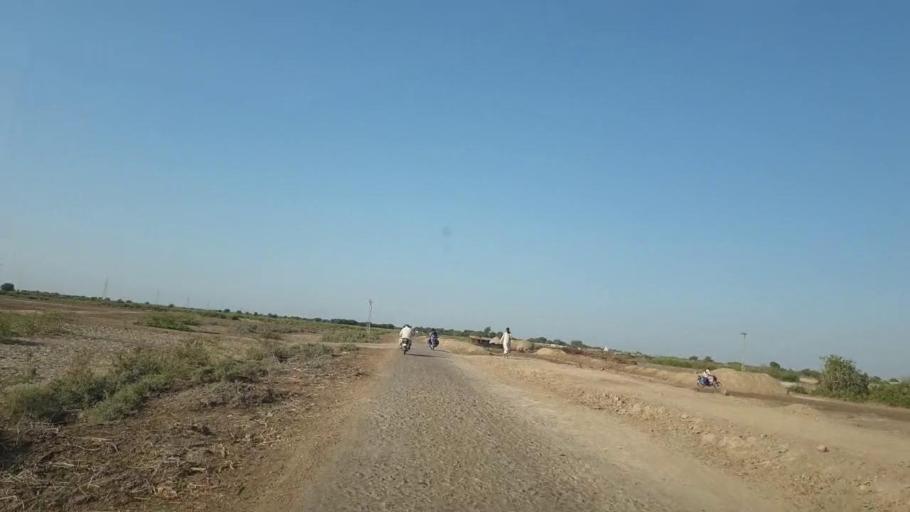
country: PK
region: Sindh
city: Naukot
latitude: 25.0410
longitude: 69.4421
